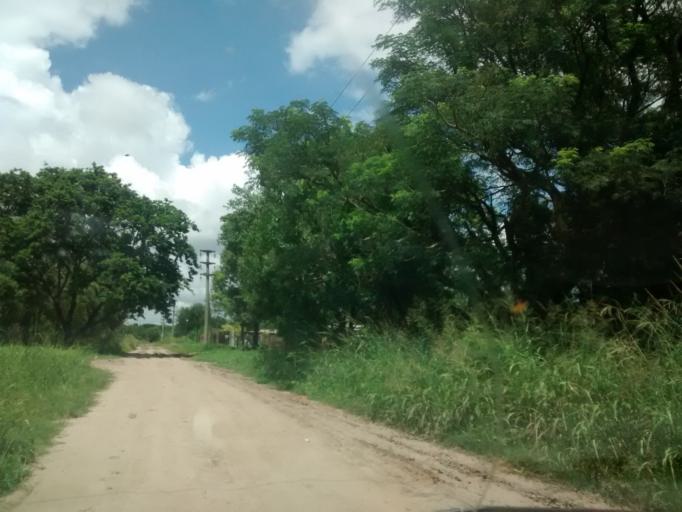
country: AR
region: Chaco
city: Fontana
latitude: -27.4107
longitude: -58.9849
